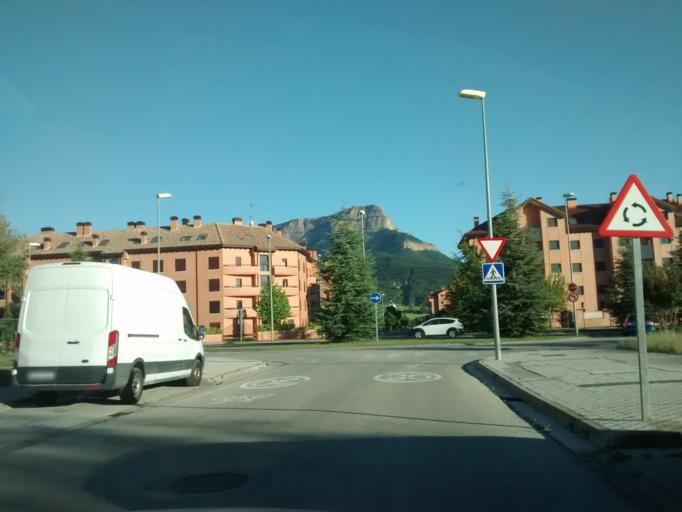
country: ES
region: Aragon
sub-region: Provincia de Huesca
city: Jaca
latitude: 42.5658
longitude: -0.5615
